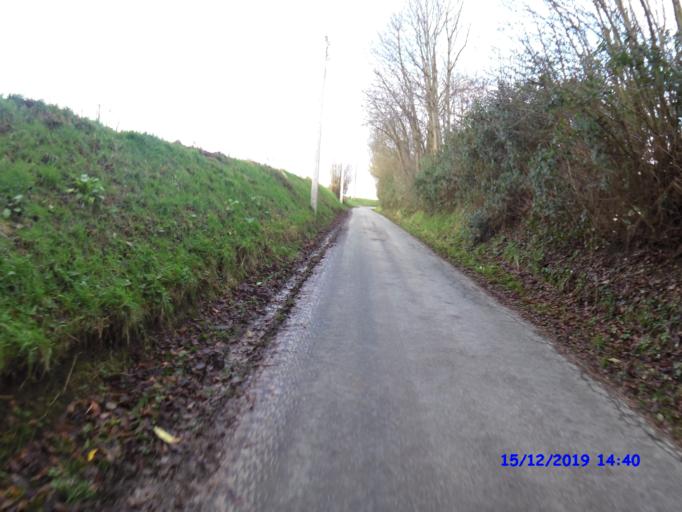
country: BE
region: Flanders
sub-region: Provincie Vlaams-Brabant
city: Beersel
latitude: 50.7413
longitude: 4.3124
